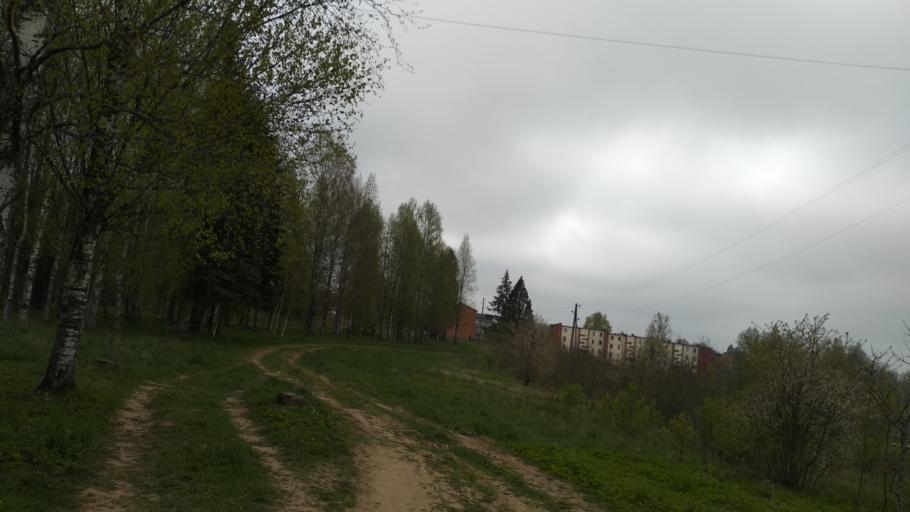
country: LV
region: Malpils
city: Malpils
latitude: 57.0149
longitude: 24.9524
